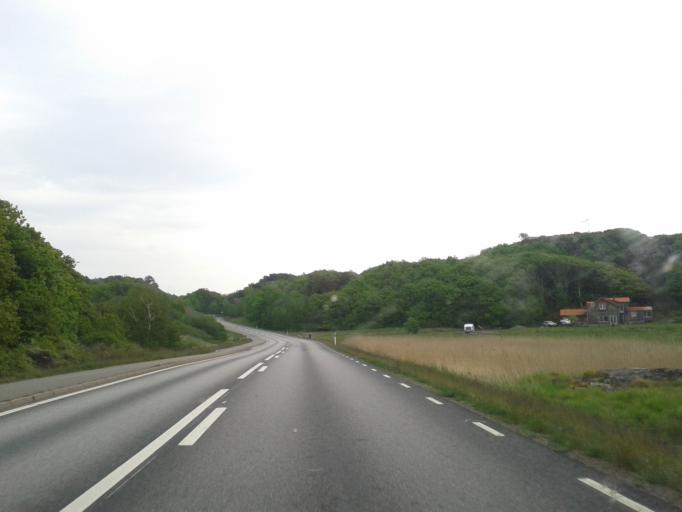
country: SE
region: Vaestra Goetaland
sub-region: Kungalvs Kommun
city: Marstrand
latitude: 57.8936
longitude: 11.6371
